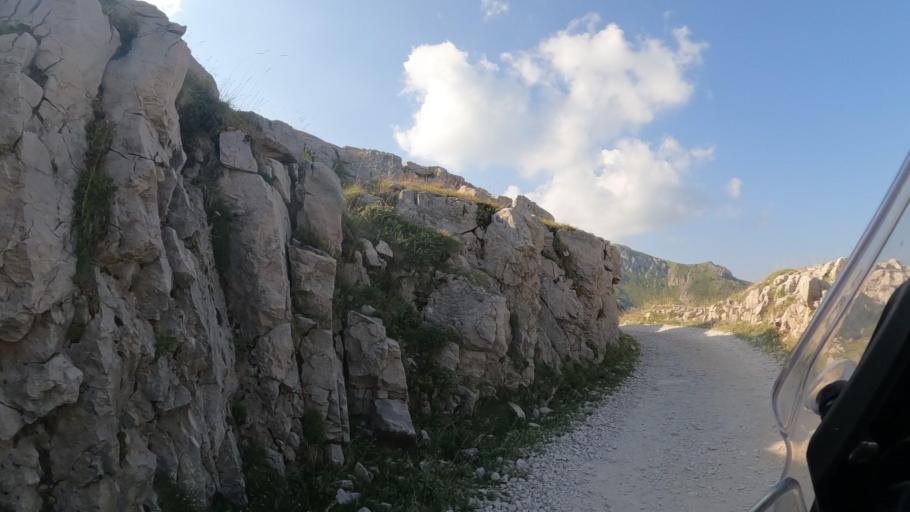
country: IT
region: Piedmont
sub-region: Provincia di Cuneo
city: Limone Piemonte
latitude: 44.1648
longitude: 7.6691
